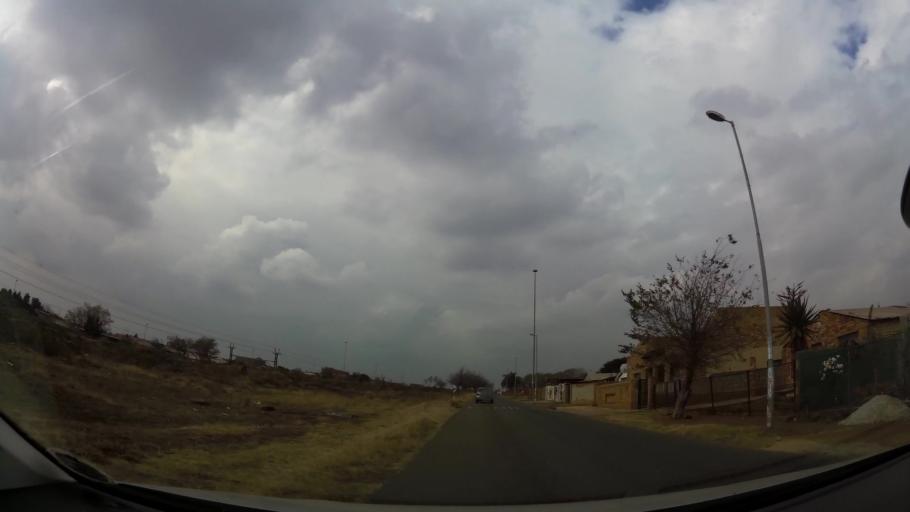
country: ZA
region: Gauteng
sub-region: City of Johannesburg Metropolitan Municipality
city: Soweto
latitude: -26.2609
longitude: 27.8510
